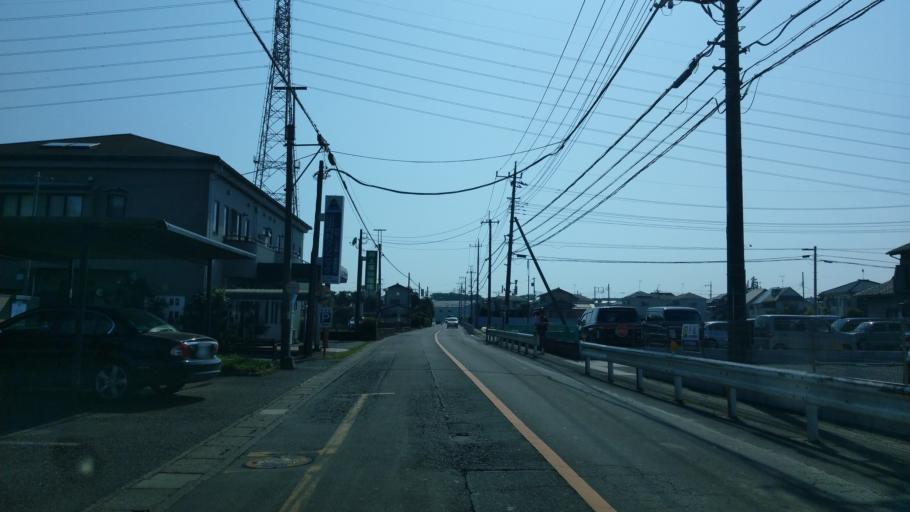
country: JP
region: Saitama
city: Oi
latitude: 35.8496
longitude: 139.5063
